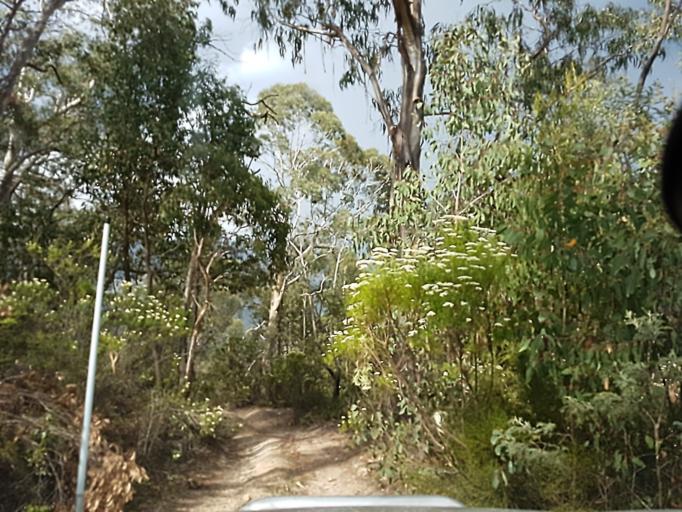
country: AU
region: New South Wales
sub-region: Snowy River
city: Jindabyne
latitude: -36.8806
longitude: 148.2148
